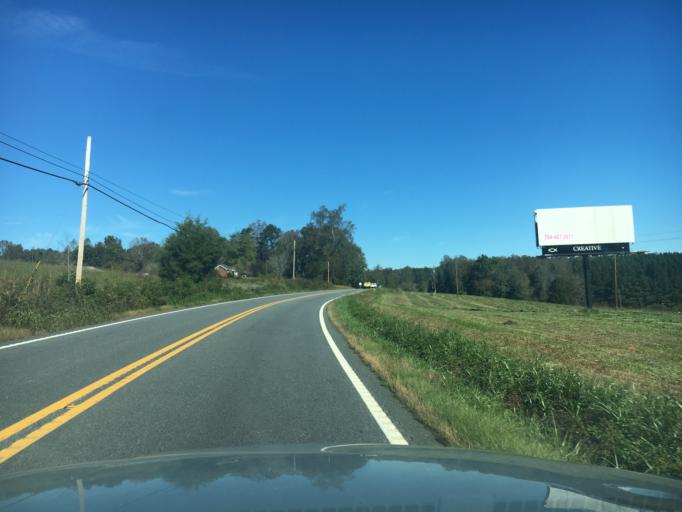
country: US
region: North Carolina
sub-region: Rutherford County
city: Spindale
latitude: 35.4048
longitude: -81.9244
